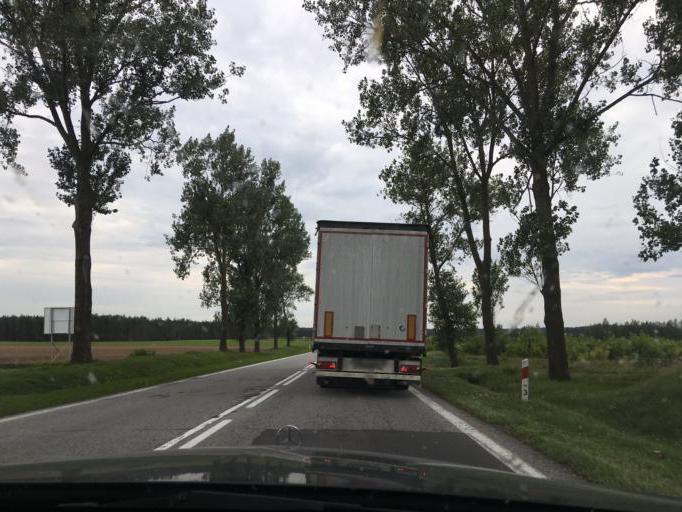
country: PL
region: Podlasie
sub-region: Powiat kolnenski
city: Stawiski
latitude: 53.3255
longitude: 22.1534
